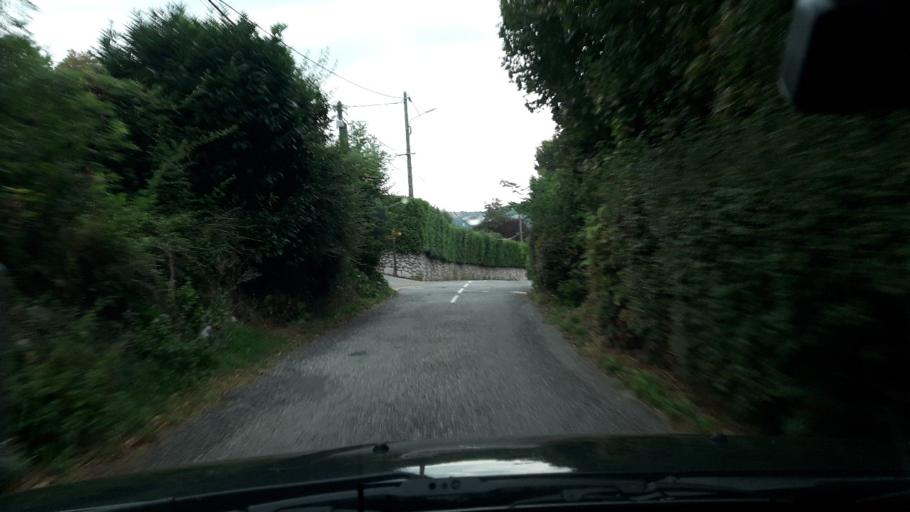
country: FR
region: Rhone-Alpes
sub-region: Departement de la Savoie
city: Barberaz
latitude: 45.5529
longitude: 5.9358
